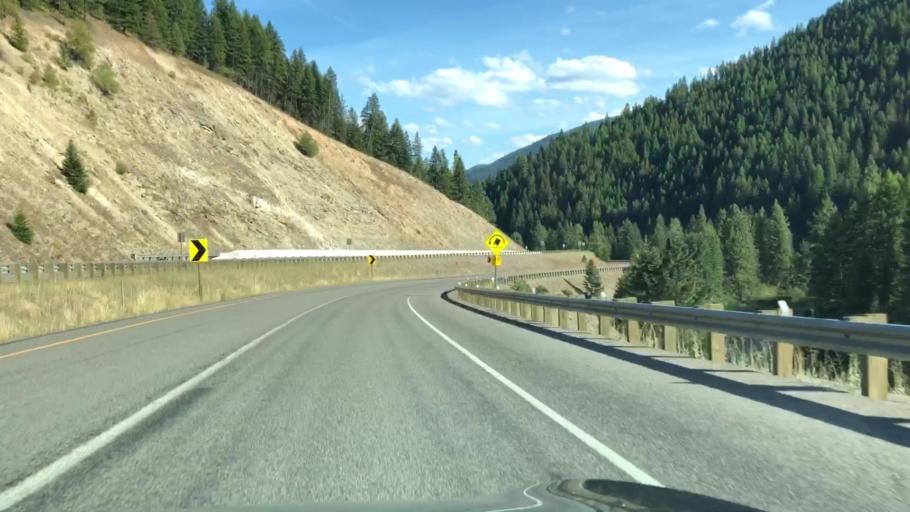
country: US
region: Montana
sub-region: Sanders County
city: Thompson Falls
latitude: 47.3344
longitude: -115.2682
